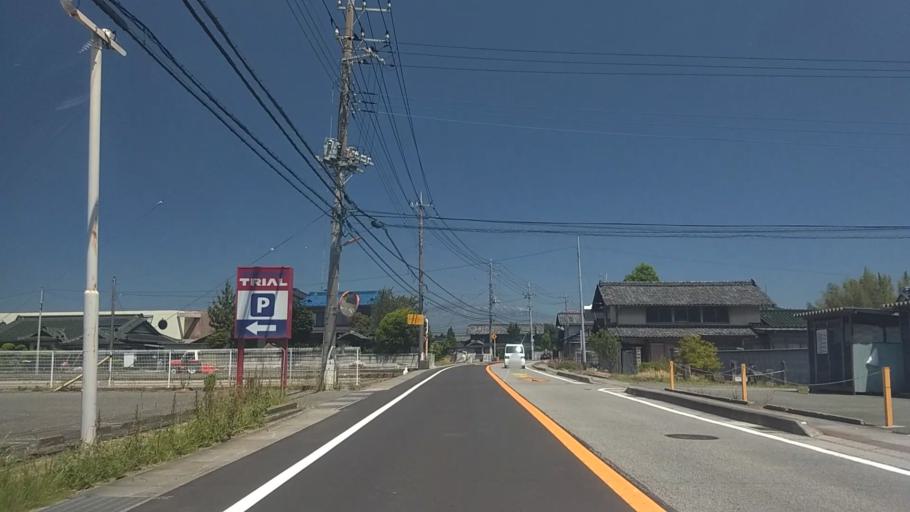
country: JP
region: Yamanashi
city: Nirasaki
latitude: 35.7251
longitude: 138.4495
